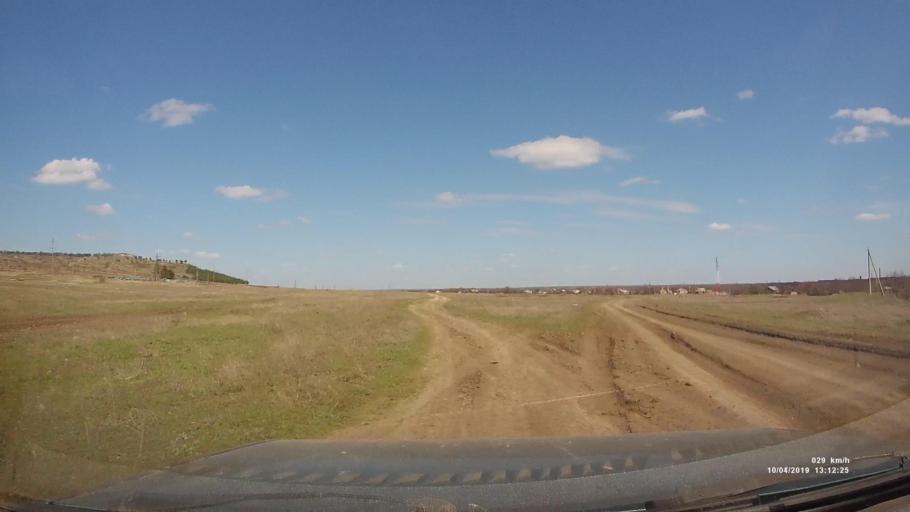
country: RU
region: Rostov
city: Masalovka
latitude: 48.4130
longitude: 40.2557
